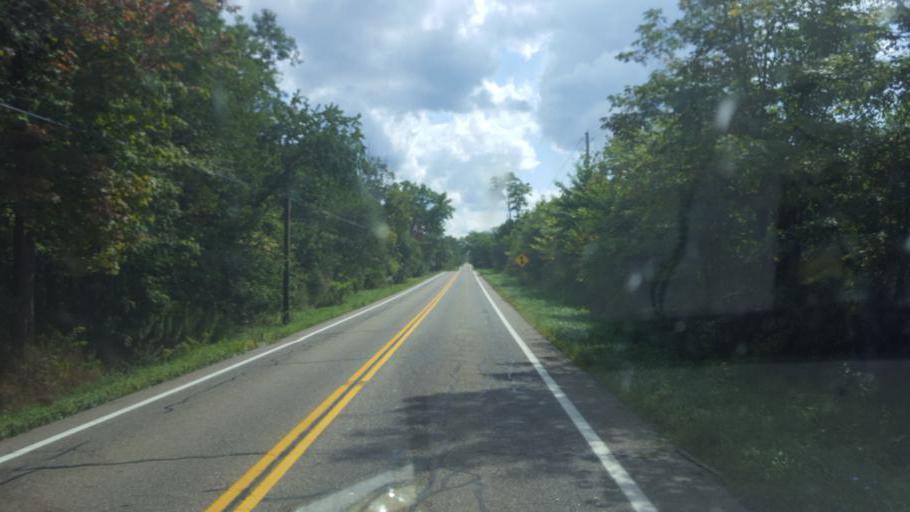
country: US
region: Ohio
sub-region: Portage County
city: Hiram
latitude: 41.3350
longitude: -81.1433
